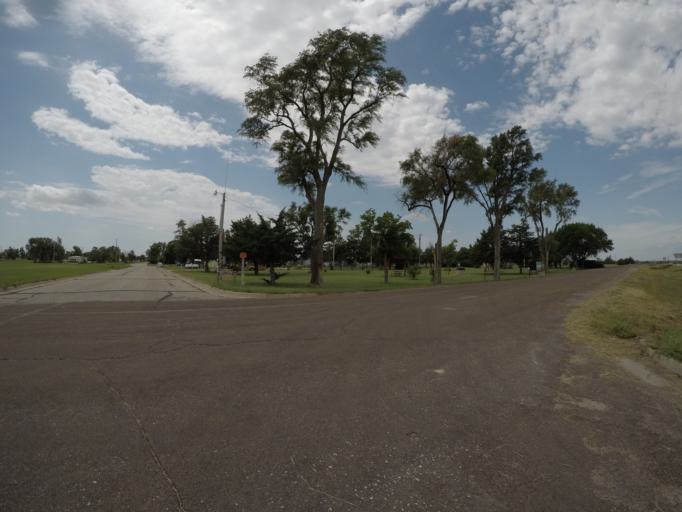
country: US
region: Kansas
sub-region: Graham County
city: Hill City
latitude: 39.3943
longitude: -99.6144
